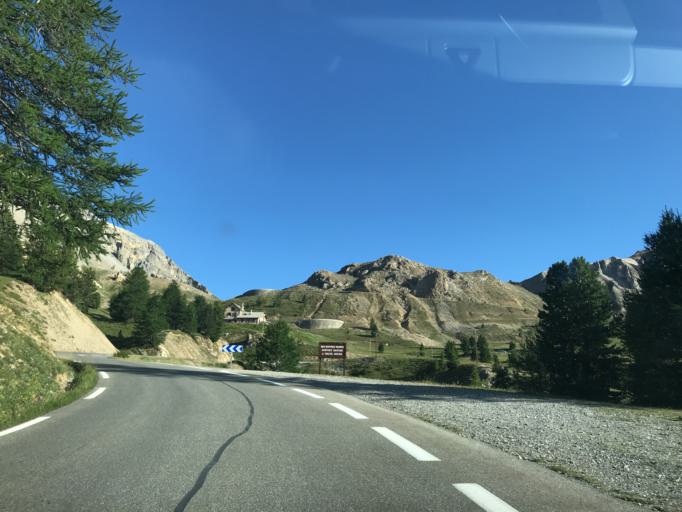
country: FR
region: Provence-Alpes-Cote d'Azur
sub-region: Departement des Hautes-Alpes
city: Villar-Saint-Pancrace
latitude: 44.8253
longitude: 6.7312
